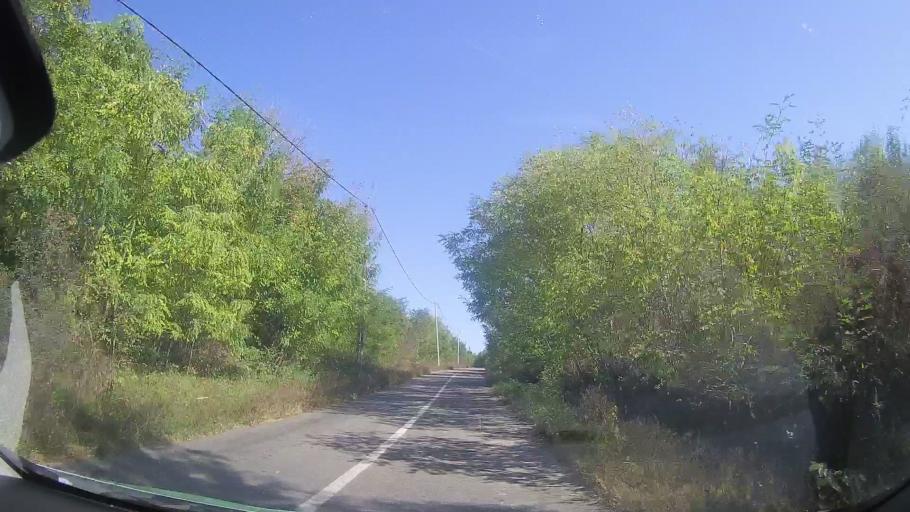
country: RO
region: Timis
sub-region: Comuna Bara
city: Bara
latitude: 45.8992
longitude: 21.8850
